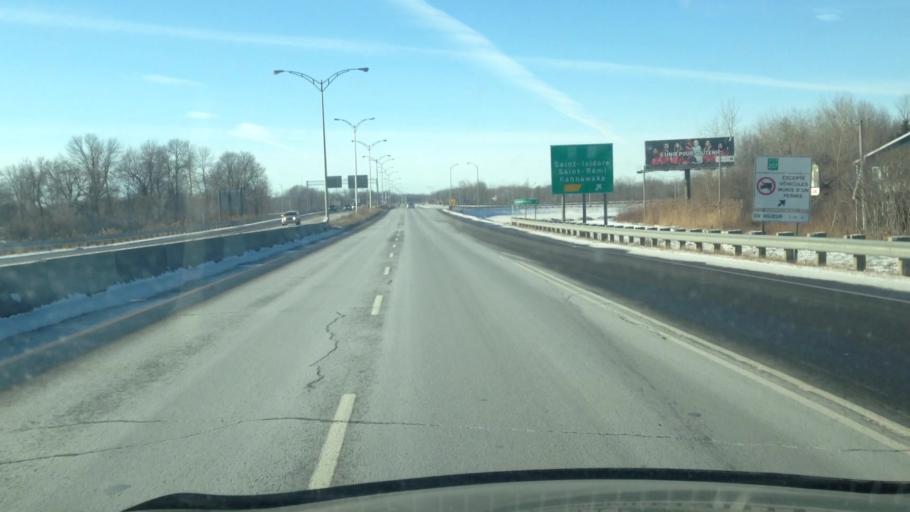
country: CA
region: Quebec
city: Montreal-Ouest
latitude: 45.4039
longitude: -73.6678
